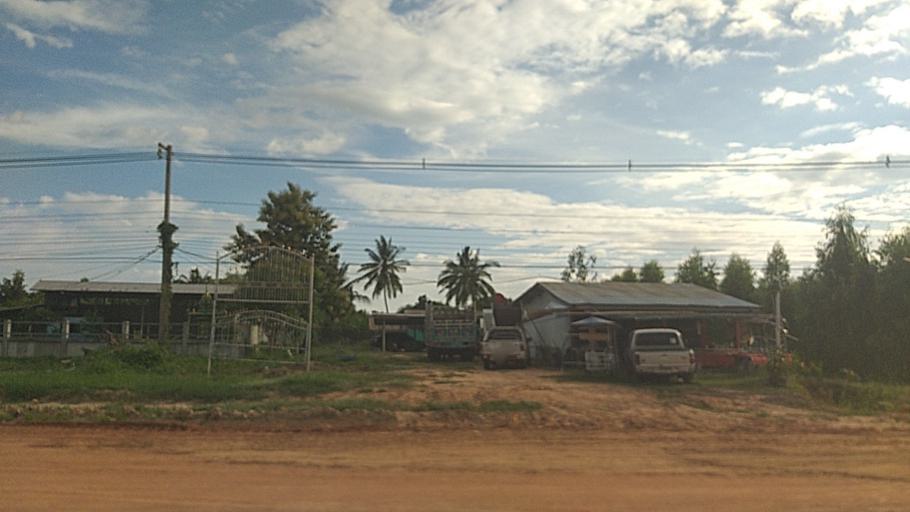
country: TH
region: Surin
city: Kap Choeng
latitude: 14.4944
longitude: 103.5700
